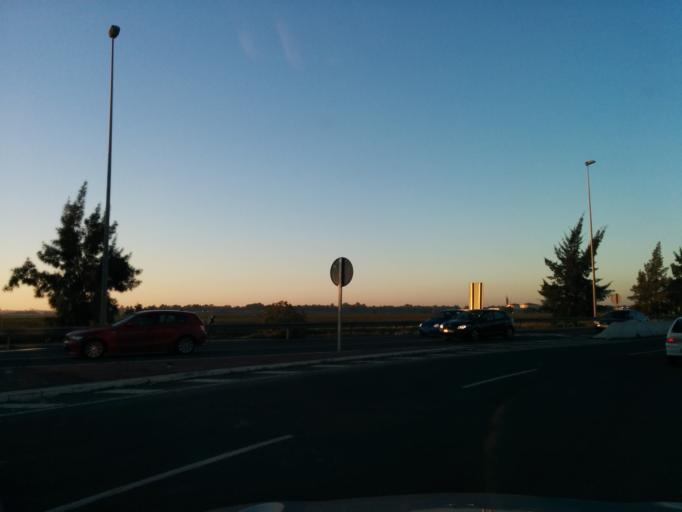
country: ES
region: Andalusia
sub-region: Provincia de Sevilla
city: Sevilla
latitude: 37.3724
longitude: -5.9247
